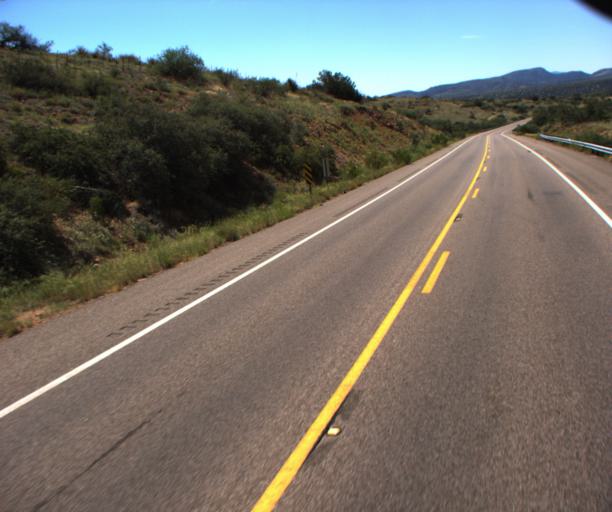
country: US
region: Arizona
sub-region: Gila County
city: Globe
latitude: 33.6044
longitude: -110.6315
